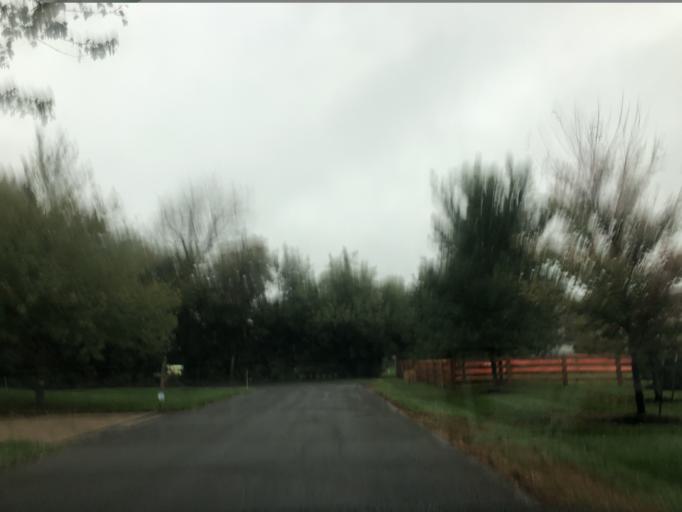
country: US
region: Ohio
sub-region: Hamilton County
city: The Village of Indian Hill
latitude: 39.2585
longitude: -84.2861
